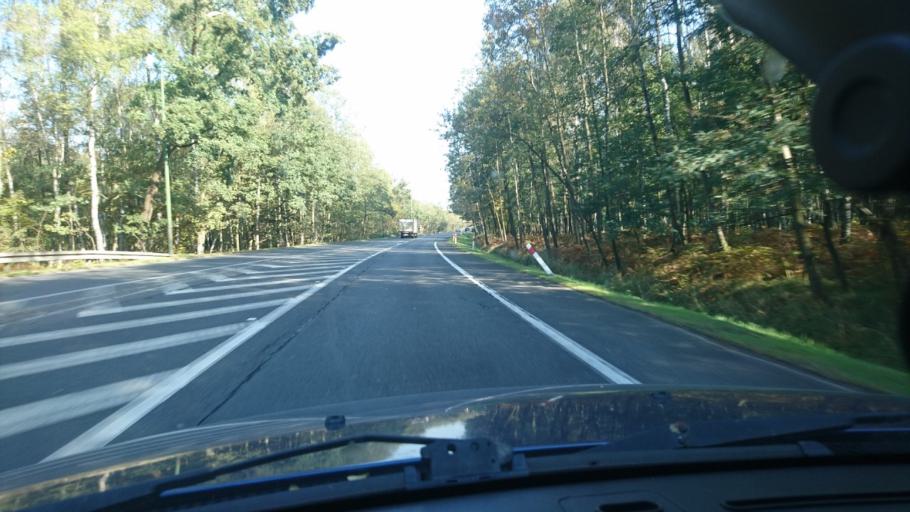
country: PL
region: Silesian Voivodeship
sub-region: Katowice
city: Murcki
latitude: 50.1663
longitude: 19.0173
